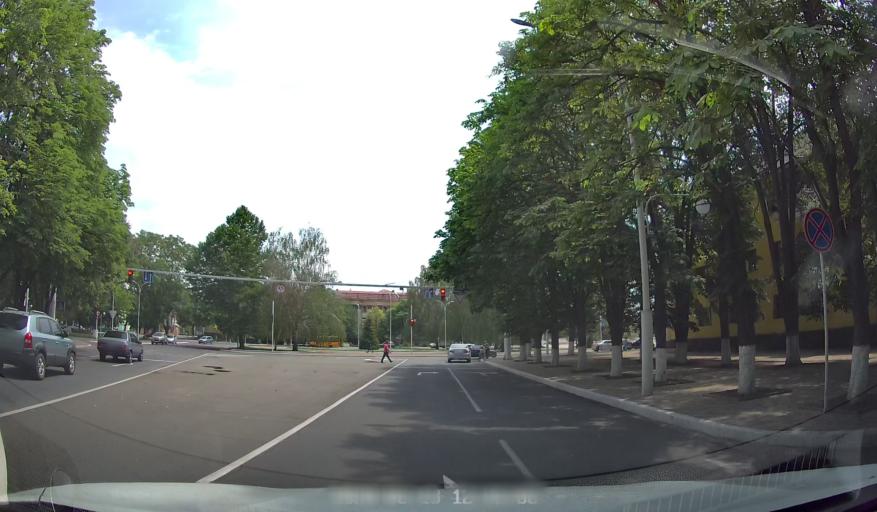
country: NG
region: Niger
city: Kutigi
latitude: 9.0697
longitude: 5.7661
